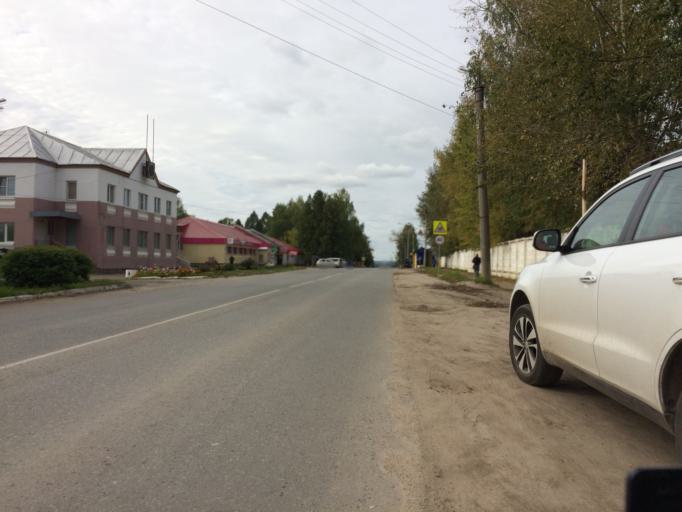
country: RU
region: Mariy-El
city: Yoshkar-Ola
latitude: 56.6535
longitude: 47.9779
